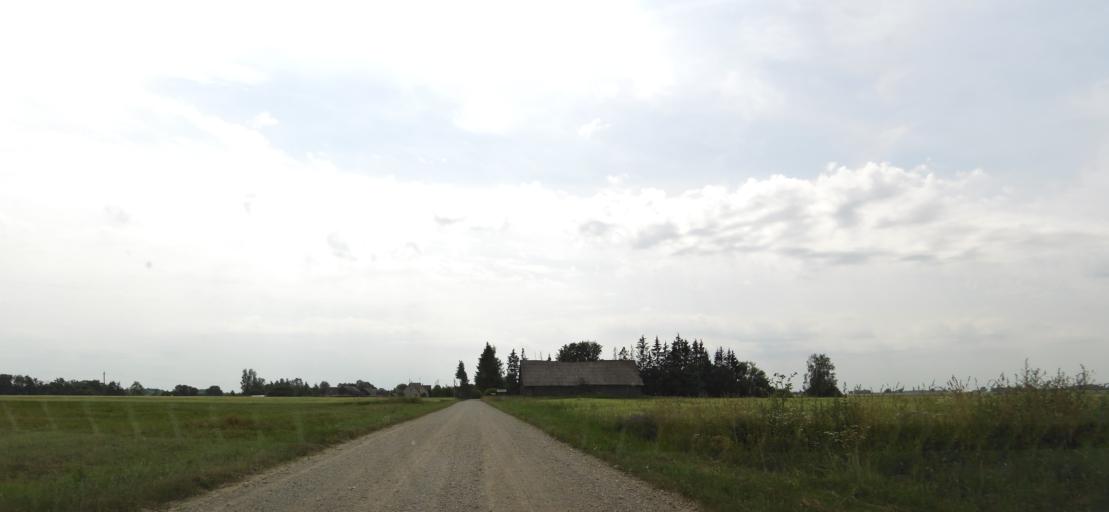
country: LT
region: Panevezys
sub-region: Birzai
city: Birzai
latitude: 56.3523
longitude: 24.7477
